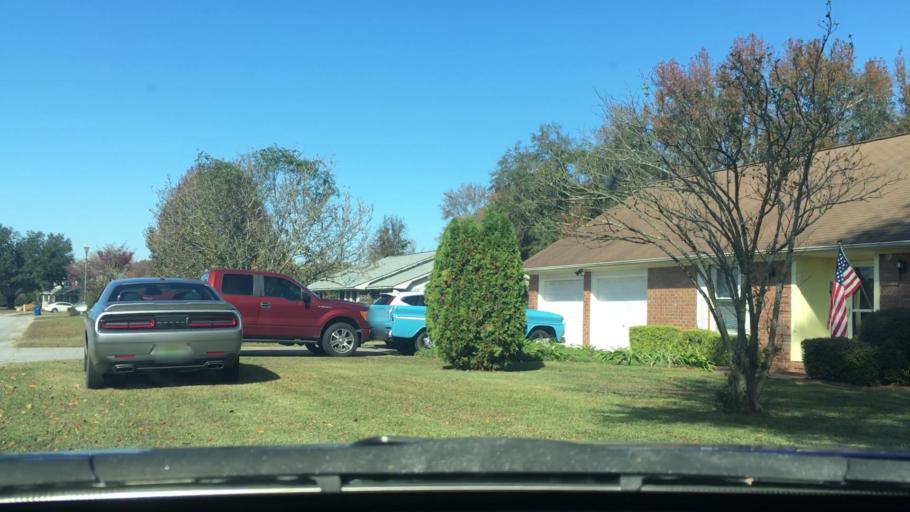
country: US
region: South Carolina
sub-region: Sumter County
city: Cane Savannah
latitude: 33.9140
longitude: -80.4114
